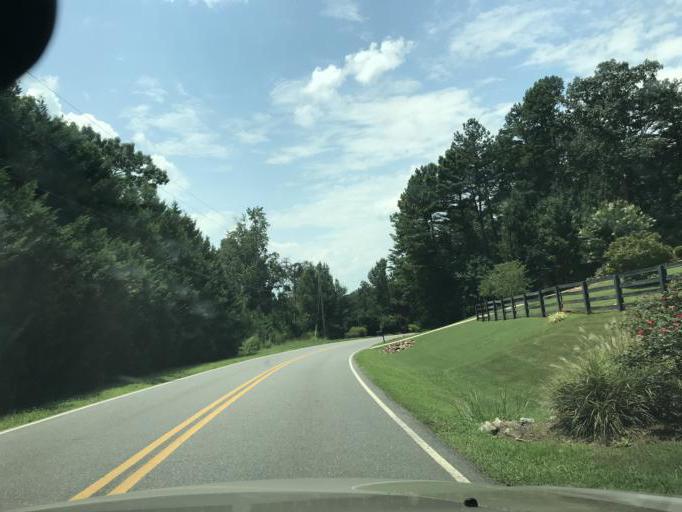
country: US
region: Georgia
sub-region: Forsyth County
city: Cumming
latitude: 34.2747
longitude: -84.1401
